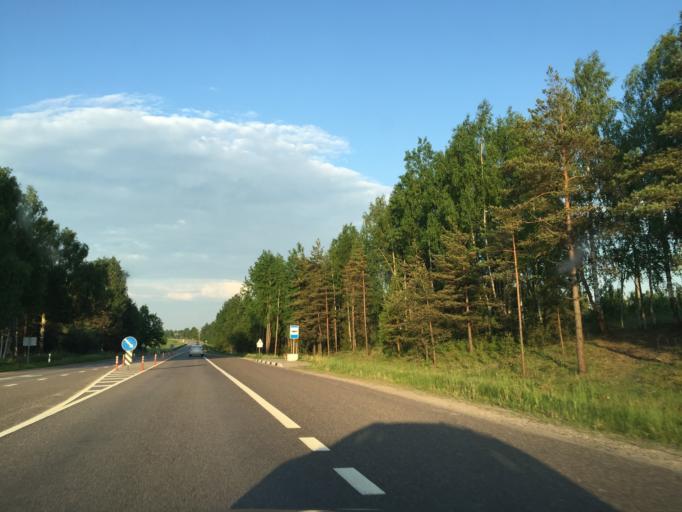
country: LT
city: Vieksniai
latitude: 55.9976
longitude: 22.4990
